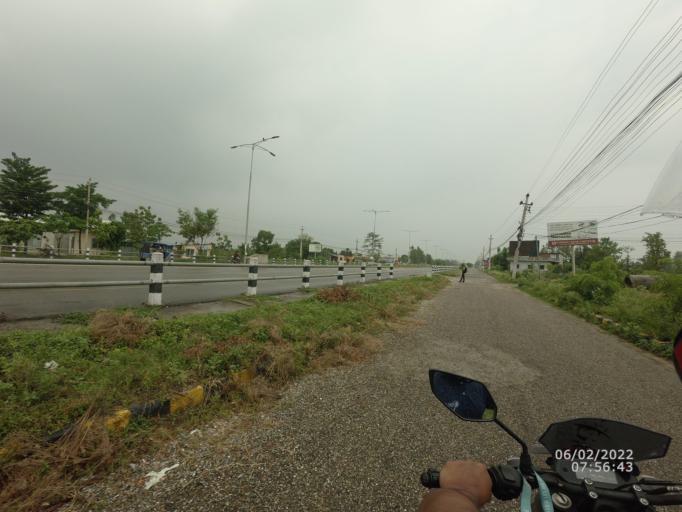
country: NP
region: Western Region
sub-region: Lumbini Zone
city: Bhairahawa
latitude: 27.4906
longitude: 83.4611
